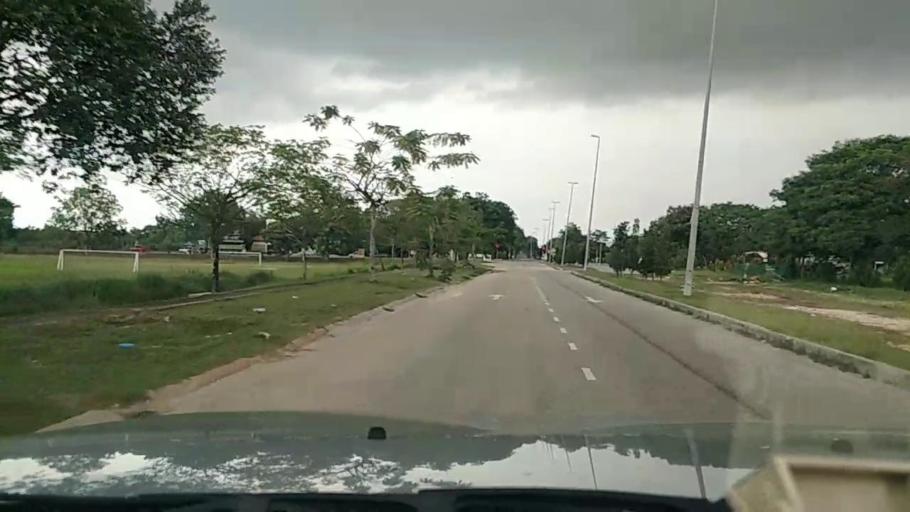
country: MY
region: Putrajaya
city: Putrajaya
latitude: 2.9378
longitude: 101.6204
